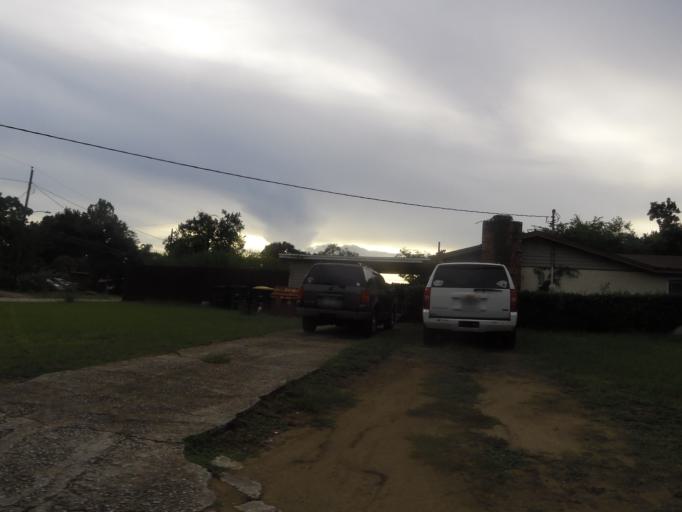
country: US
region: Florida
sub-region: Duval County
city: Neptune Beach
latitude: 30.2934
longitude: -81.5032
